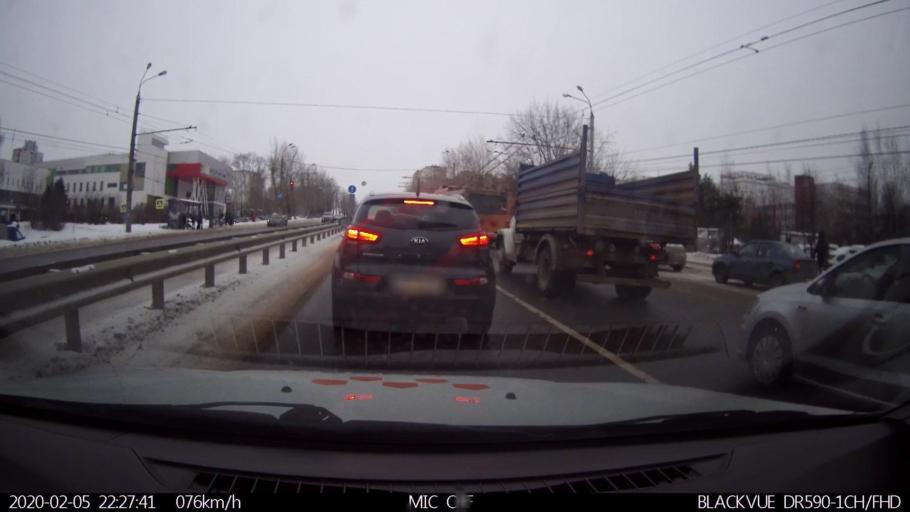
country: RU
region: Nizjnij Novgorod
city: Imeni Stepana Razina
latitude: 54.7610
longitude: 44.1187
